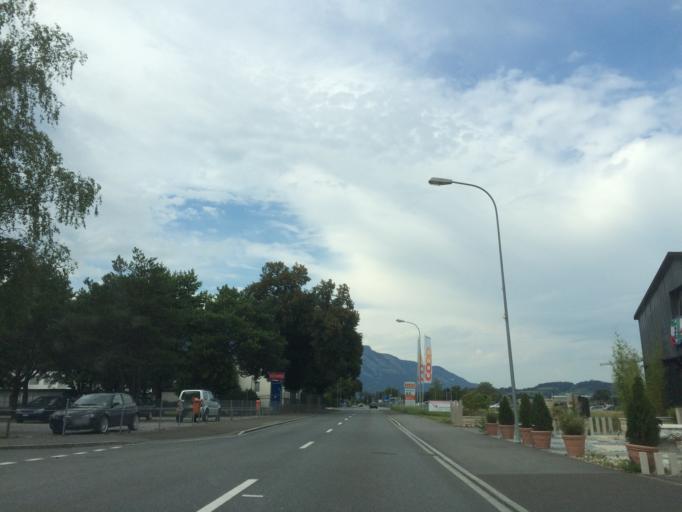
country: LI
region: Schaan
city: Schaan
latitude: 47.1743
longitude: 9.5087
